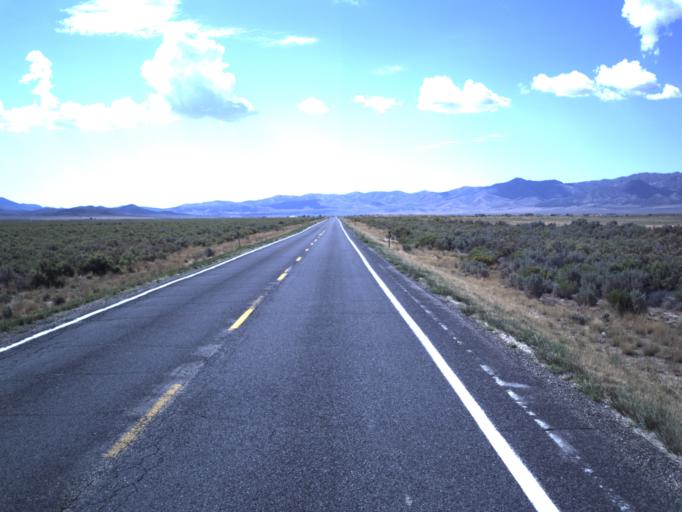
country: US
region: Utah
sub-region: Tooele County
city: Tooele
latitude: 40.1472
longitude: -112.4308
